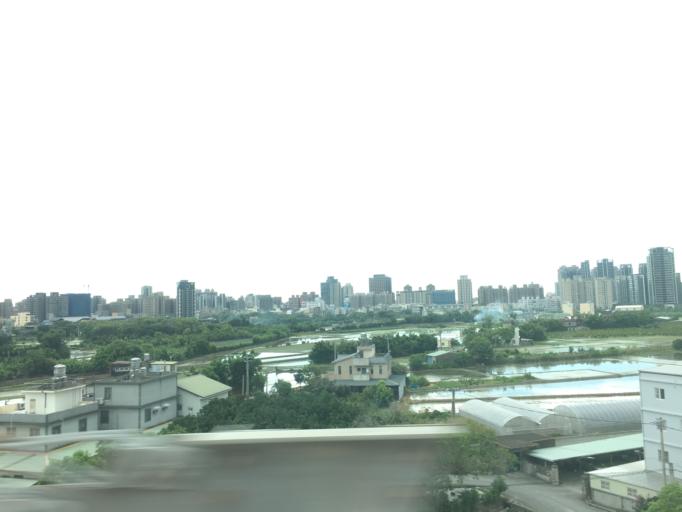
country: TW
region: Taiwan
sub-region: Hsinchu
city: Zhubei
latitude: 24.8164
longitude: 121.0423
